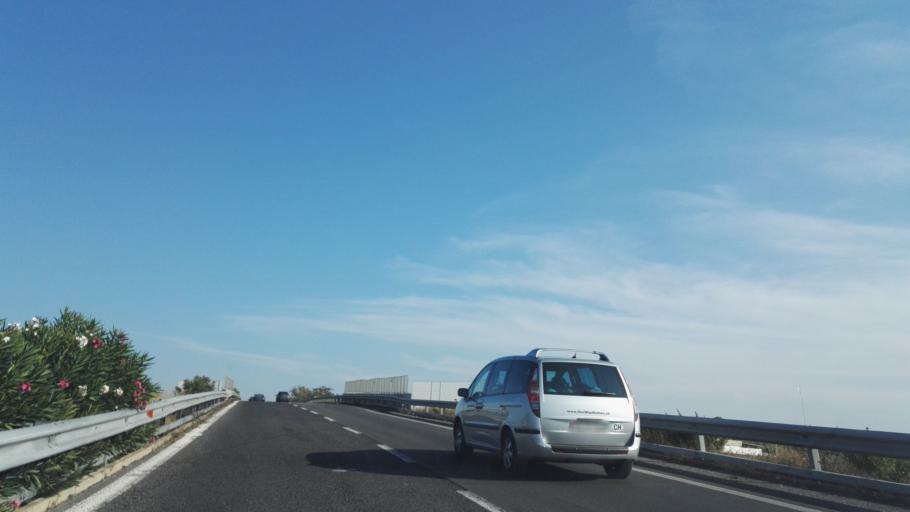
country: IT
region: Apulia
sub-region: Provincia di Bari
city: Polignano a Mare
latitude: 40.9999
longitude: 17.2005
